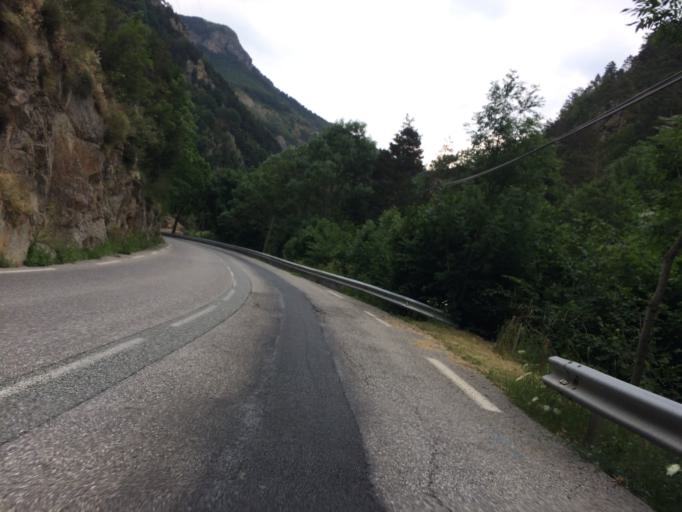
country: FR
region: Provence-Alpes-Cote d'Azur
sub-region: Departement des Alpes-Maritimes
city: Tende
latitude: 44.1028
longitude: 7.5781
